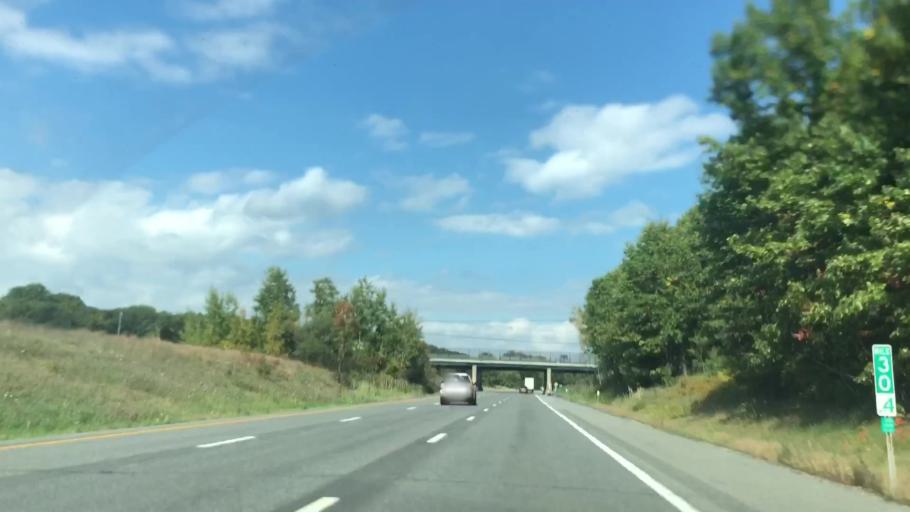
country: US
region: New York
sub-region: Saratoga County
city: Saratoga Springs
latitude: 43.0950
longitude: -73.7515
